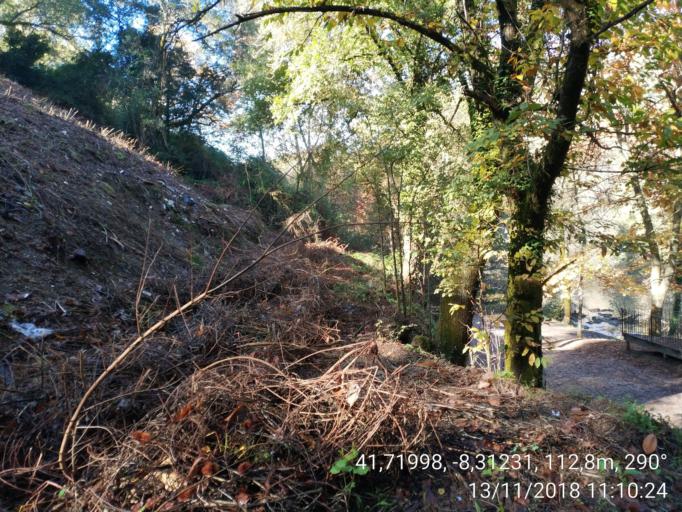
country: PT
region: Braga
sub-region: Terras de Bouro
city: Terras de Bouro
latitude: 41.7200
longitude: -8.3123
